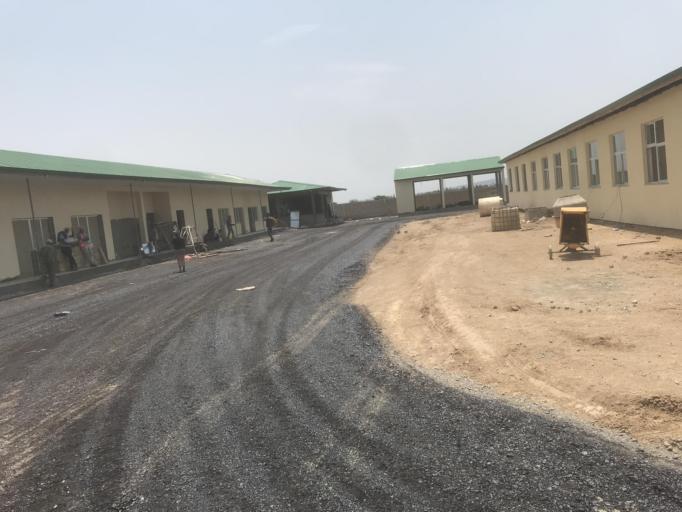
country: ET
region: Oromiya
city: Mojo
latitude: 8.3038
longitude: 38.9333
